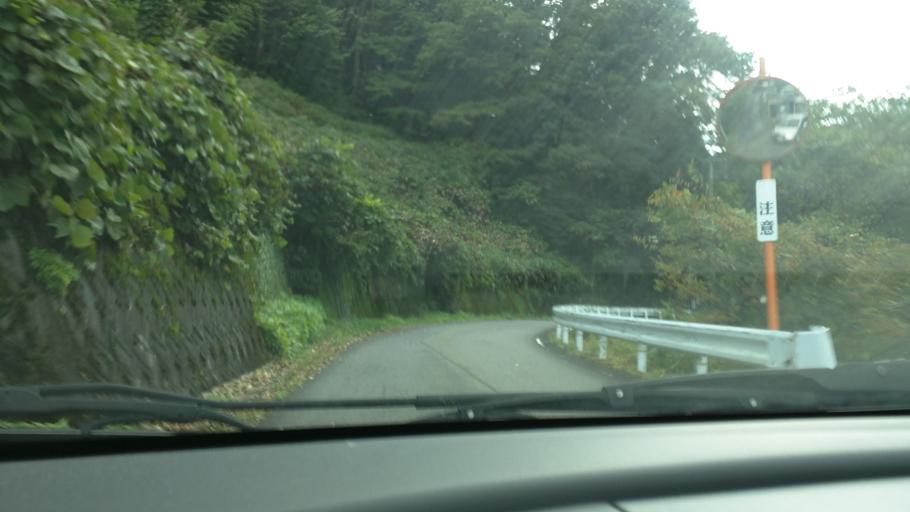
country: JP
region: Fukushima
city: Kitakata
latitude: 37.4605
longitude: 139.6958
